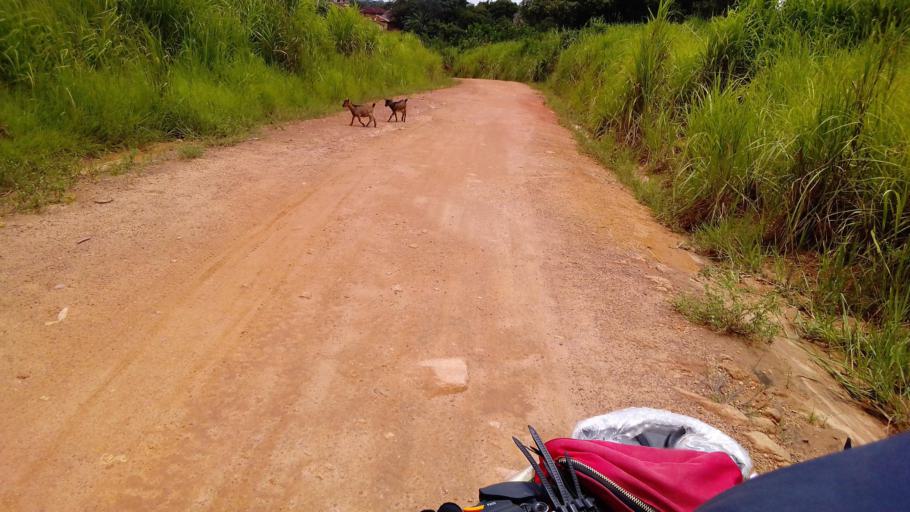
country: SL
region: Eastern Province
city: Koidu
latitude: 8.6861
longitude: -10.9305
